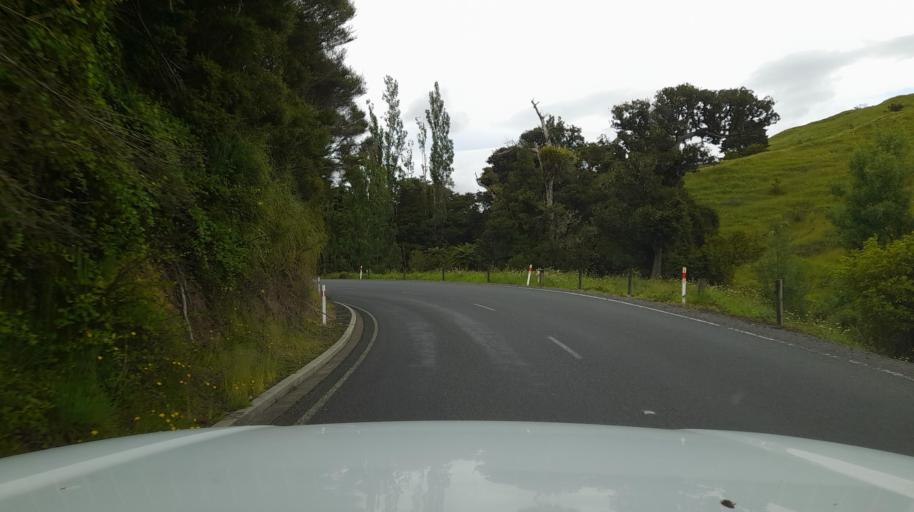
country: NZ
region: Northland
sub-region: Far North District
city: Kaitaia
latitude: -35.3035
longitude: 173.3595
